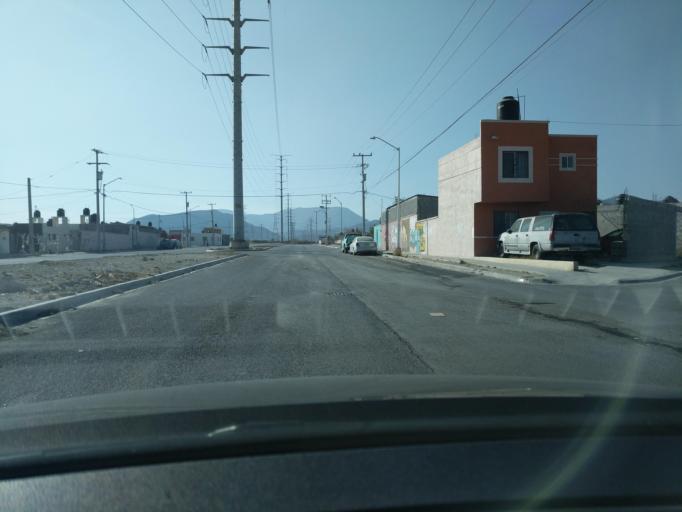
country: MX
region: Coahuila
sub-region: Ramos Arizpe
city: Ramos Arizpe
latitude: 25.5430
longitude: -100.9716
